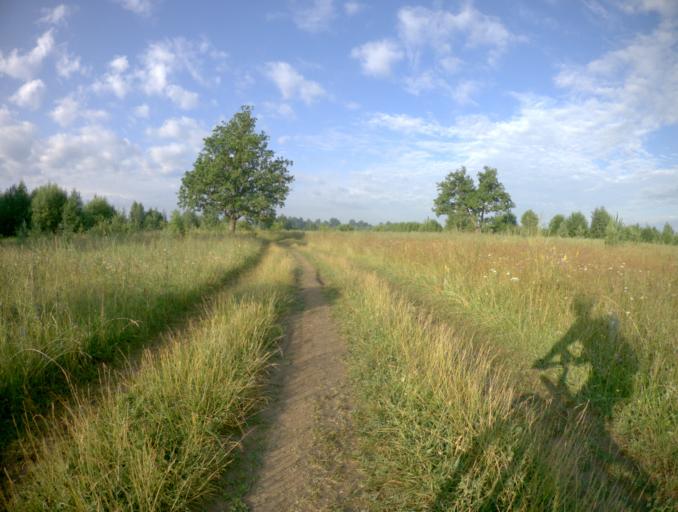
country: RU
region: Vladimir
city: Galitsy
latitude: 56.1795
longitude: 42.8070
